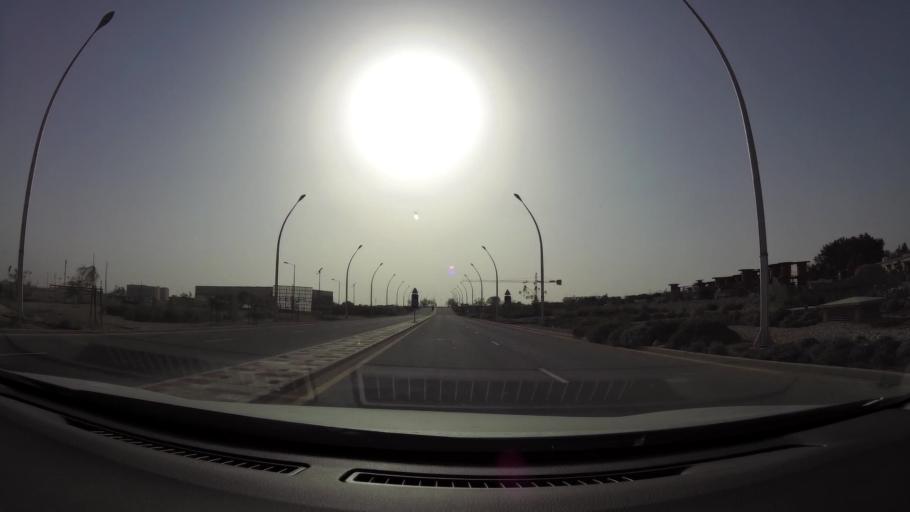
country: QA
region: Baladiyat ar Rayyan
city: Ar Rayyan
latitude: 25.3273
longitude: 51.4339
